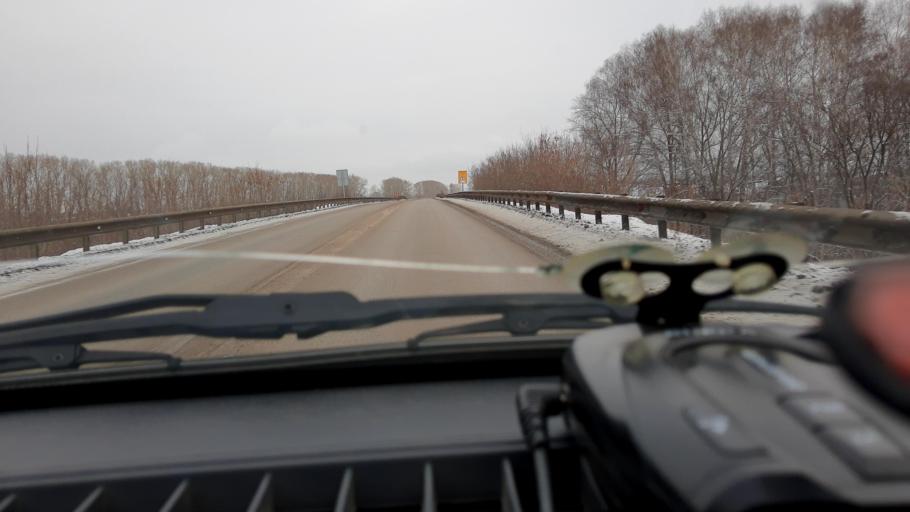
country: RU
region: Bashkortostan
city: Ufa
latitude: 54.6101
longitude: 55.8800
